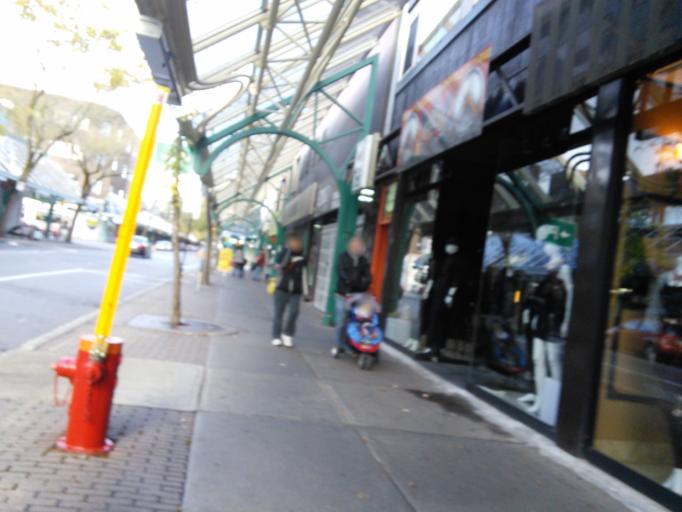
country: CA
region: Quebec
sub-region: Montreal
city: Montreal
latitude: 45.5388
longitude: -73.6093
